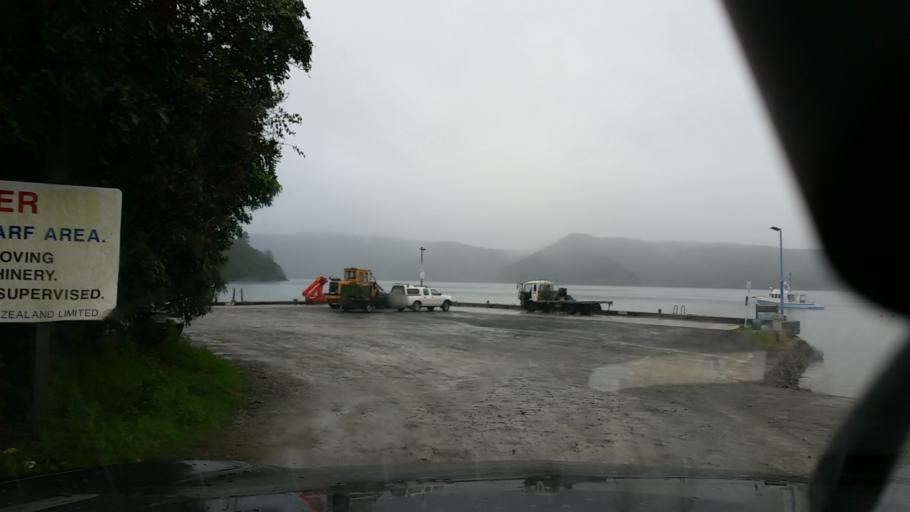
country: NZ
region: Marlborough
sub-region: Marlborough District
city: Picton
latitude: -41.3014
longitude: 174.1143
